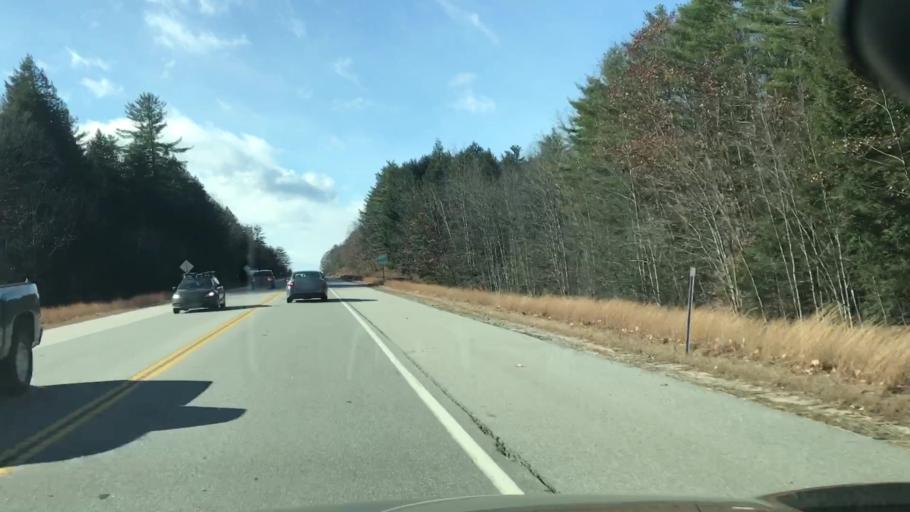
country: US
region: New Hampshire
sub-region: Belknap County
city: Barnstead
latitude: 43.3433
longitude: -71.2711
